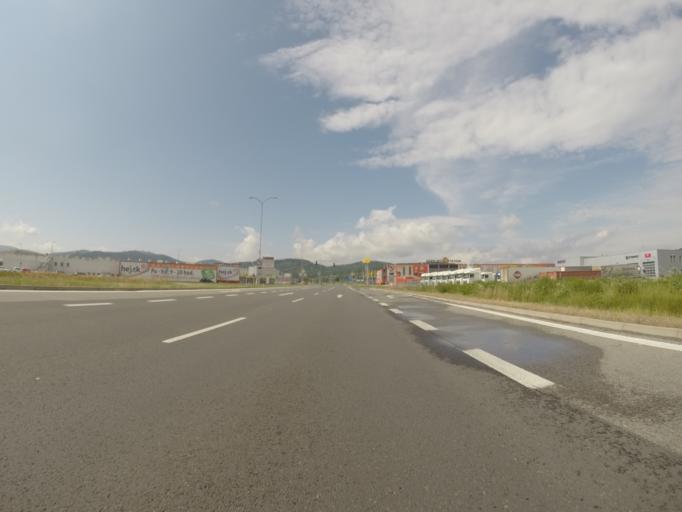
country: SK
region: Banskobystricky
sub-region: Okres Banska Bystrica
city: Zvolen
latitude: 48.5867
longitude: 19.1073
